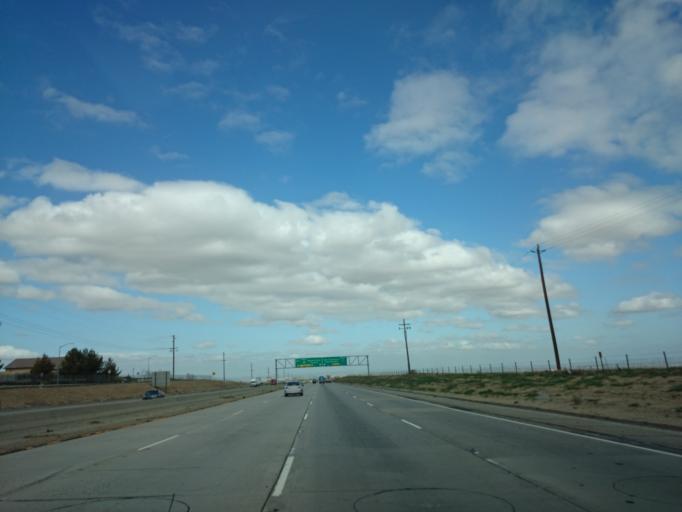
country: US
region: California
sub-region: Kern County
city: Frazier Park
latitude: 34.9930
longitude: -118.9473
